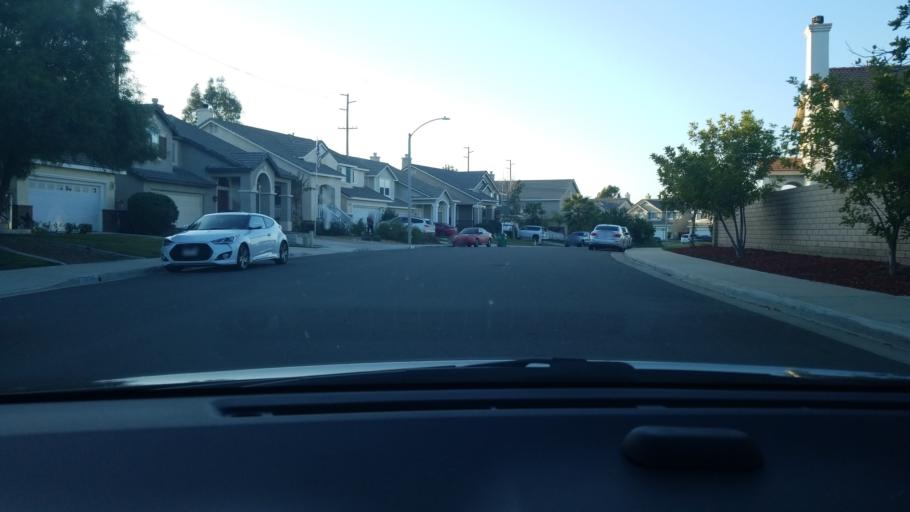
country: US
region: California
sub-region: Riverside County
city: Murrieta Hot Springs
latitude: 33.5489
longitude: -117.1341
